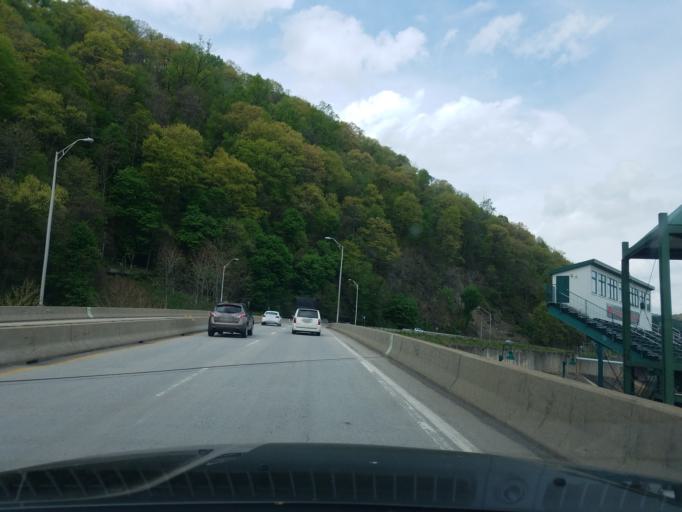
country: US
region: Pennsylvania
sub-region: Cambria County
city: Johnstown
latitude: 40.3282
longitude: -78.9254
